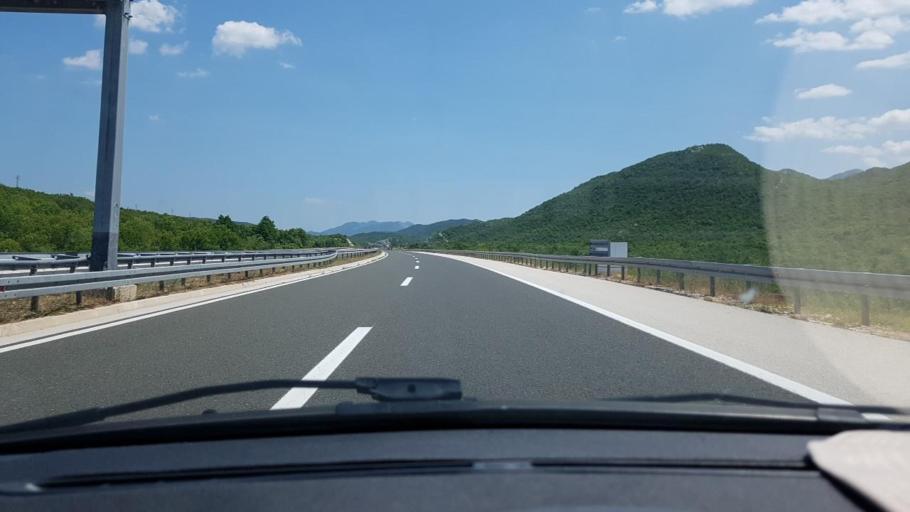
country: HR
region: Splitsko-Dalmatinska
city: Grubine
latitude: 43.3632
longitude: 17.0963
